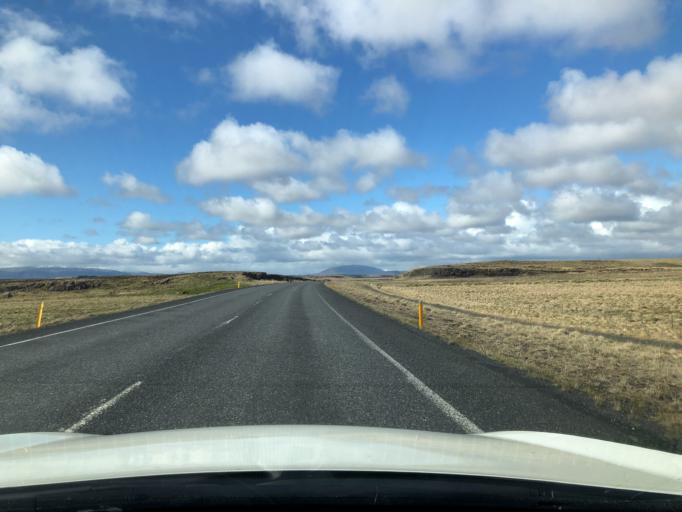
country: IS
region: South
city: Selfoss
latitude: 63.9216
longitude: -20.6555
